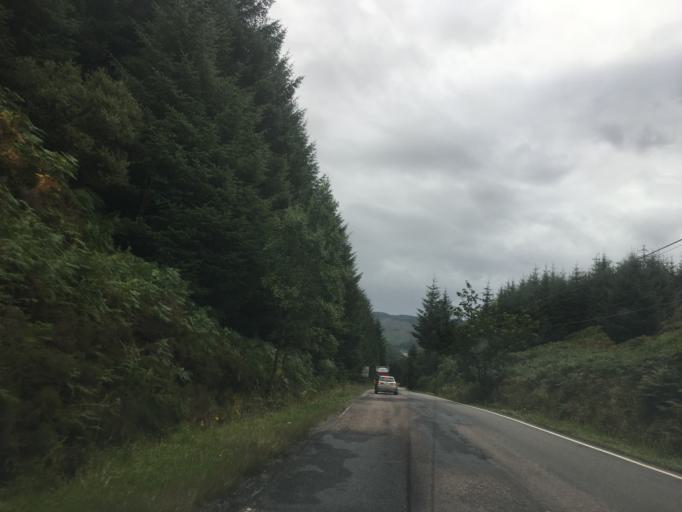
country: GB
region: Scotland
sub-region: Argyll and Bute
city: Oban
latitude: 56.2825
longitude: -5.4821
